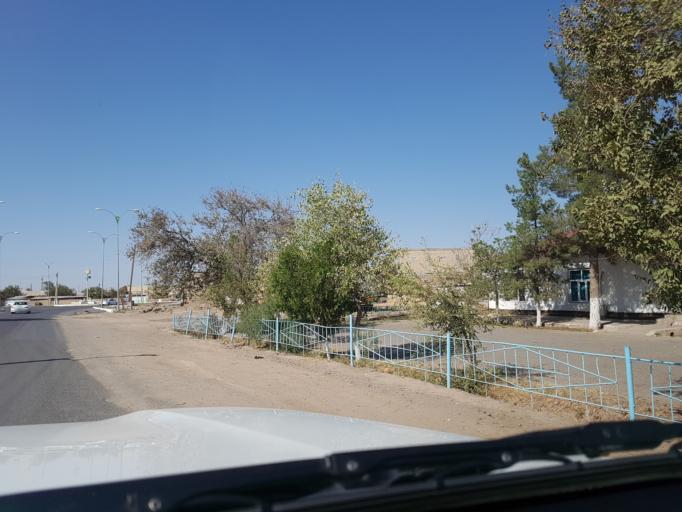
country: IR
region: Razavi Khorasan
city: Sarakhs
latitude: 36.5224
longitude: 61.2175
